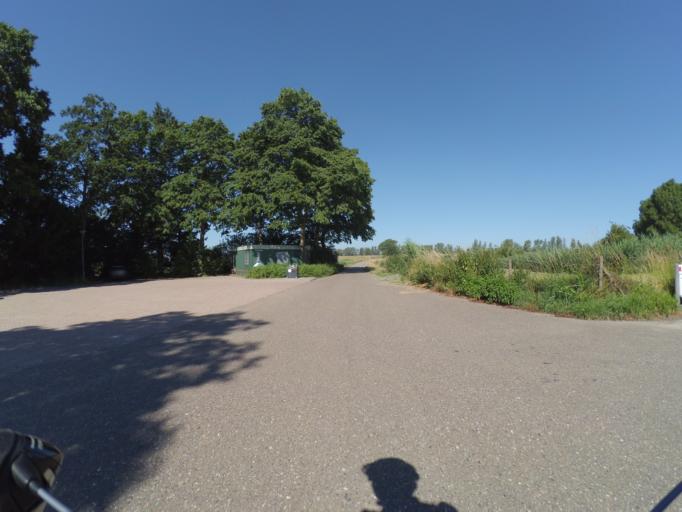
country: NL
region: South Holland
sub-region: Gemeente Dordrecht
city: Dordrecht
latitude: 51.7153
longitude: 4.6902
